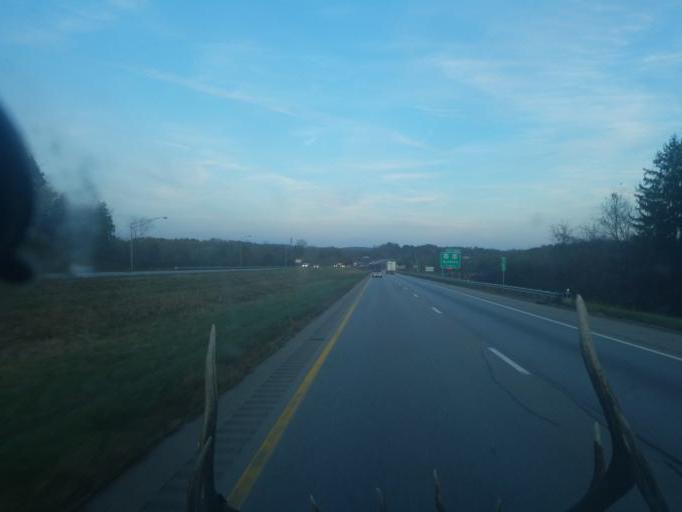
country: US
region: Ohio
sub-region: Muskingum County
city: Pleasant Grove
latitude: 39.9734
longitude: -81.8563
